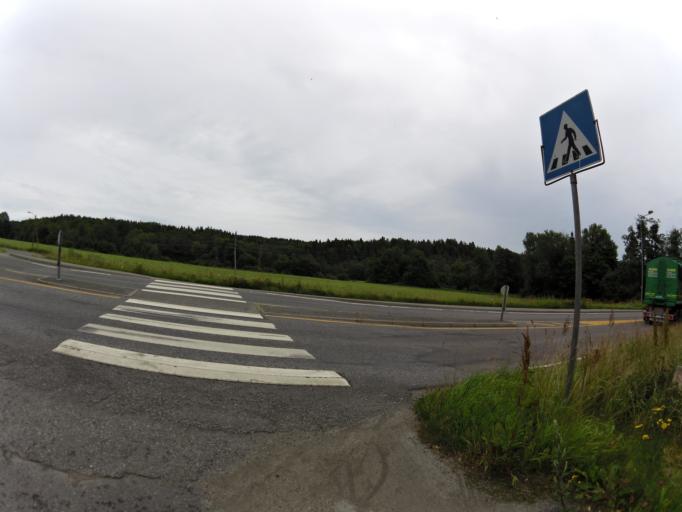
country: NO
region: Ostfold
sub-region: Moss
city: Moss
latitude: 59.4771
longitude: 10.6941
